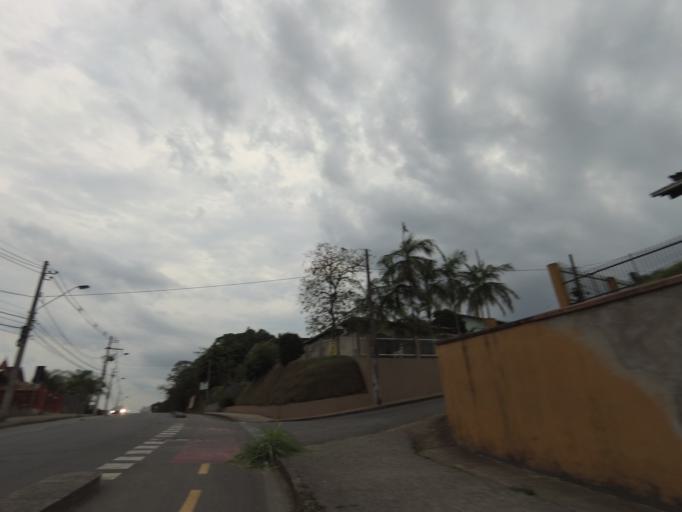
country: BR
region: Santa Catarina
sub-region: Blumenau
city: Blumenau
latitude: -26.8808
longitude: -49.0620
